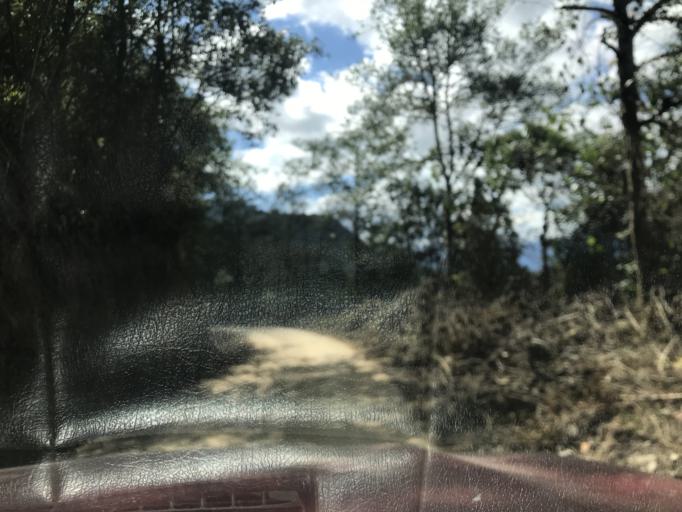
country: PE
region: Cajamarca
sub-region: Provincia de Chota
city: Querocoto
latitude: -6.3457
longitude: -79.0516
